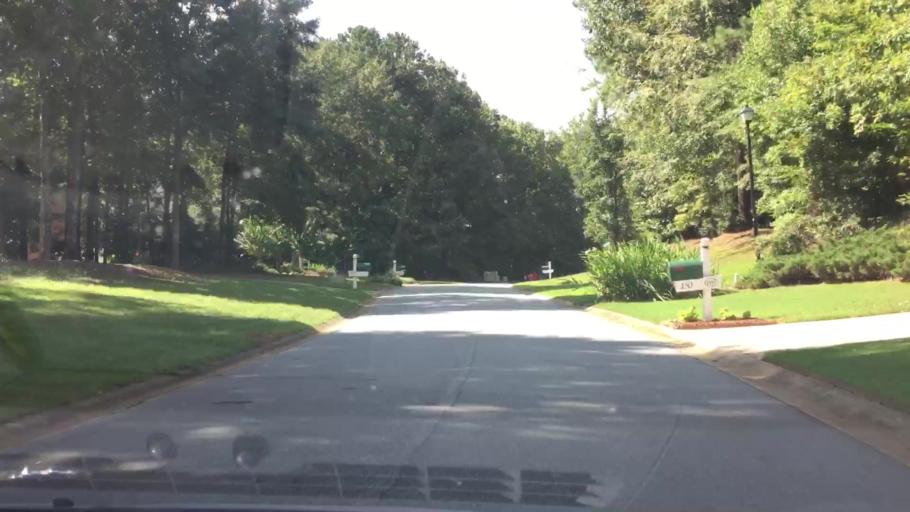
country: US
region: Georgia
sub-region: Coweta County
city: Senoia
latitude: 33.3588
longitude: -84.5193
